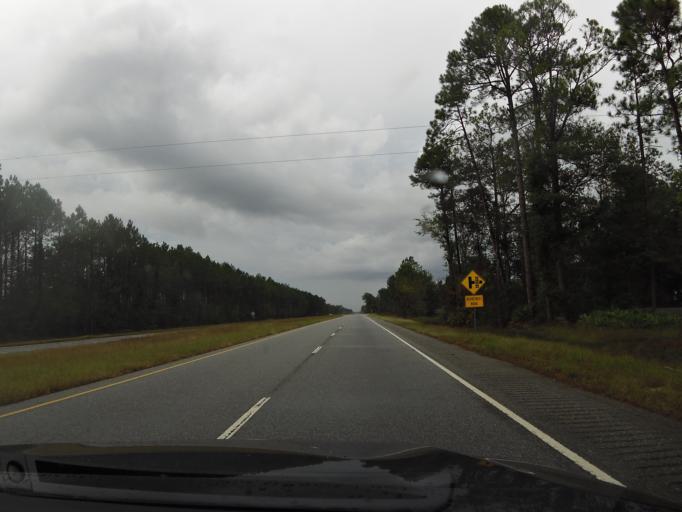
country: US
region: Georgia
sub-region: Wayne County
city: Jesup
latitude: 31.5230
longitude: -81.7810
